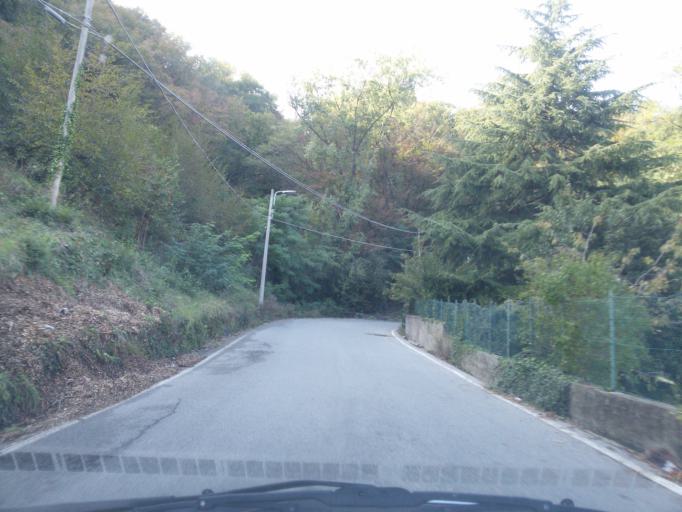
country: IT
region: Liguria
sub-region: Provincia di Genova
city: Piccarello
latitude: 44.4617
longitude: 8.9672
